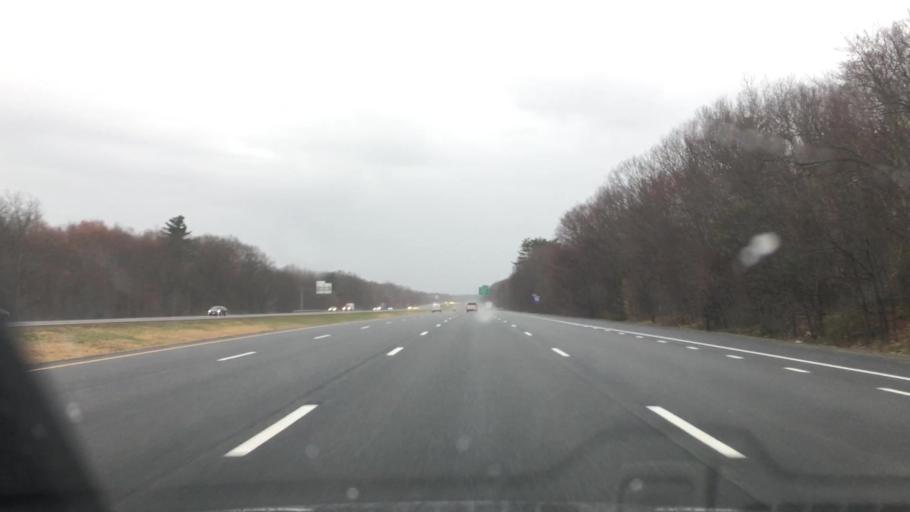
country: US
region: Massachusetts
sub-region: Essex County
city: West Newbury
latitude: 42.7743
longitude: -70.9305
